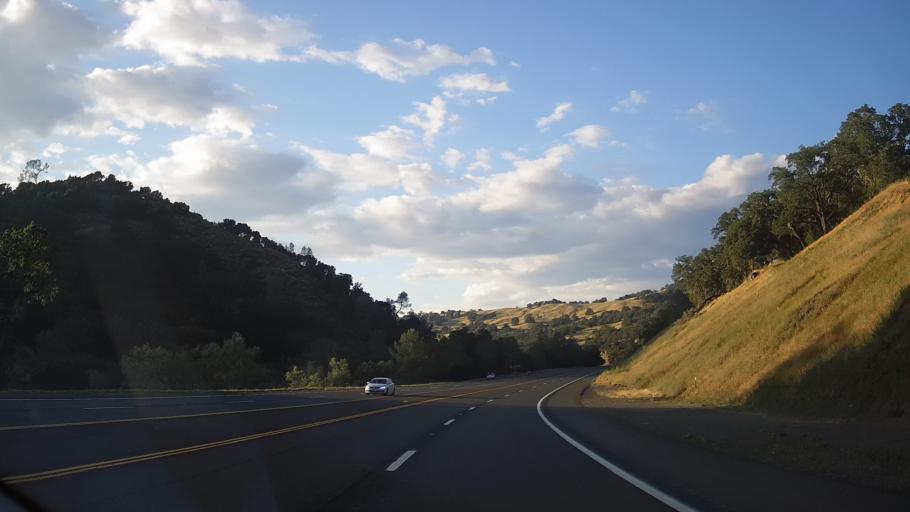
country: US
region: California
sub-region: Sonoma County
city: Cloverdale
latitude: 38.9189
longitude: -123.0585
